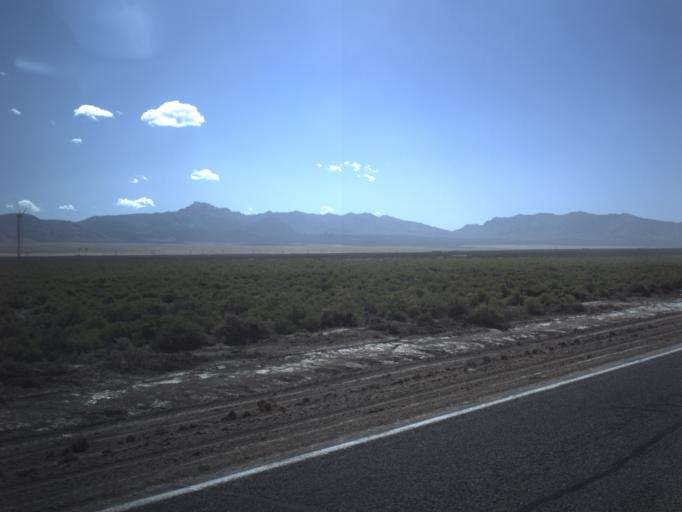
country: US
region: Utah
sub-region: Beaver County
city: Milford
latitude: 38.5164
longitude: -112.9912
